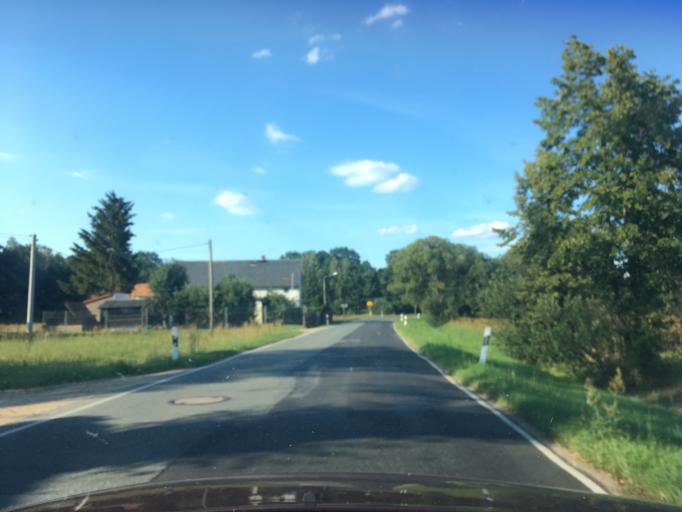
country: PL
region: Lower Silesian Voivodeship
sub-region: Powiat zgorzelecki
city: Piensk
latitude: 51.2222
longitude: 15.0042
